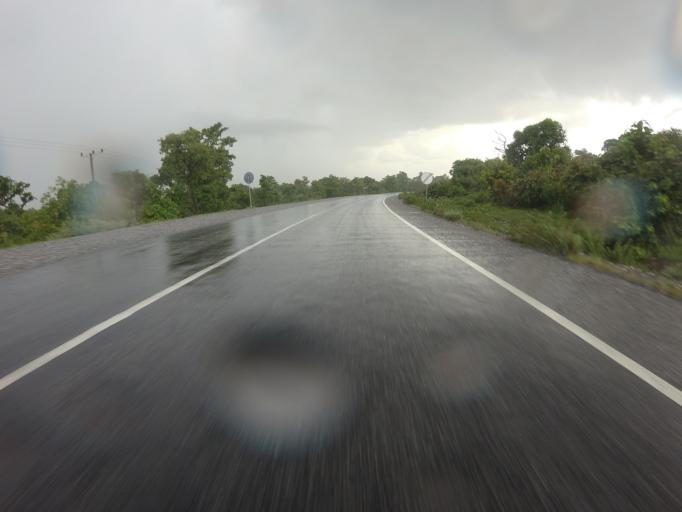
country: GH
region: Northern
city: Tamale
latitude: 9.1325
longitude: -1.5854
